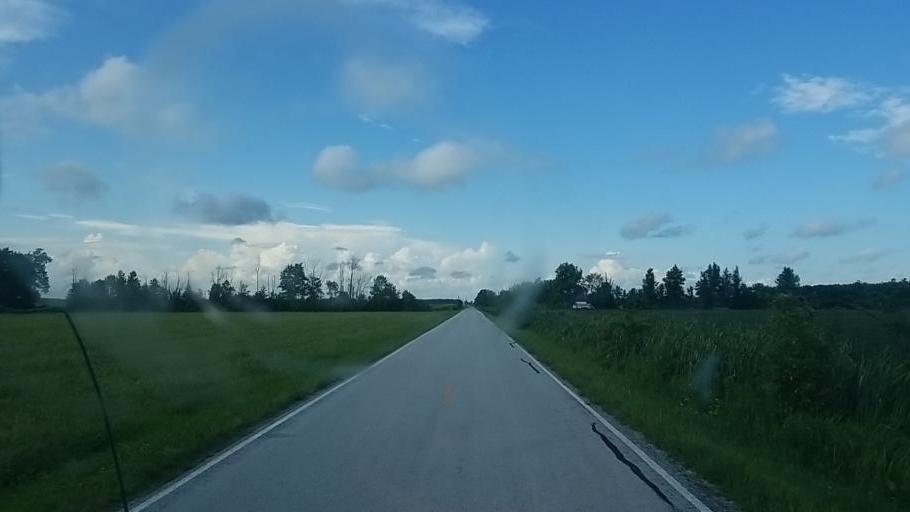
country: US
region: Ohio
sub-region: Hardin County
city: Forest
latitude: 40.7503
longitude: -83.4966
